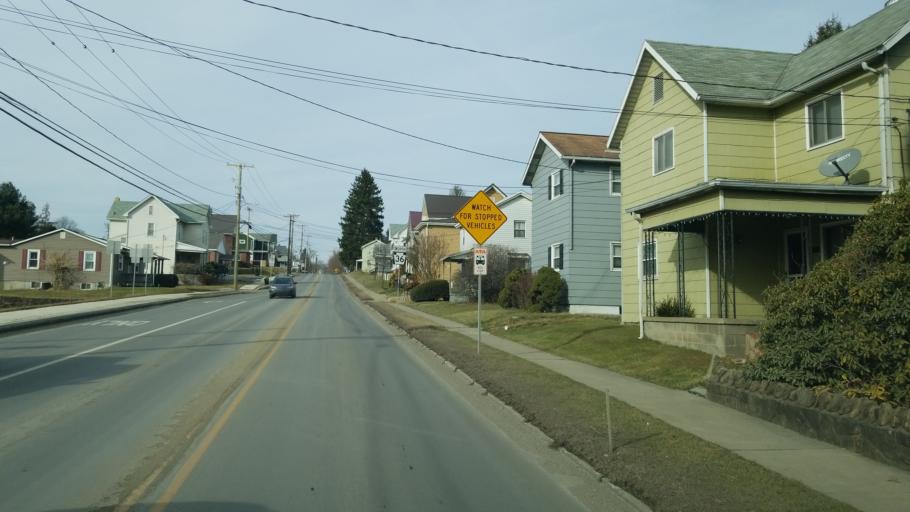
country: US
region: Pennsylvania
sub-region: Jefferson County
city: Punxsutawney
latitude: 40.9440
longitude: -78.9918
